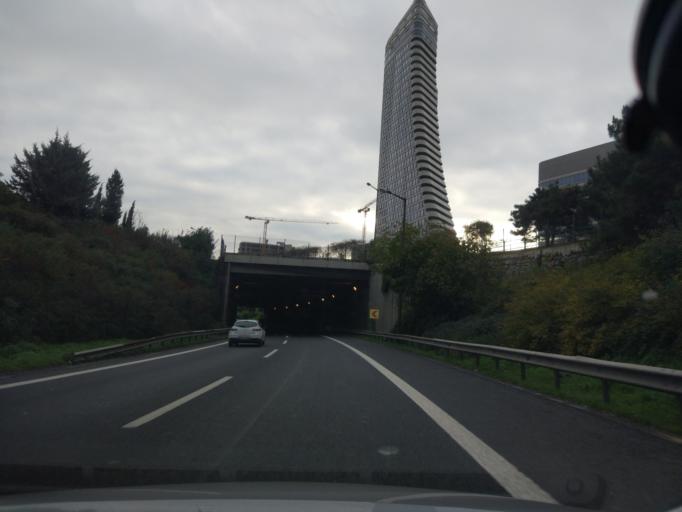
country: TR
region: Istanbul
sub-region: Atasehir
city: Atasehir
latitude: 40.9963
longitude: 29.1219
